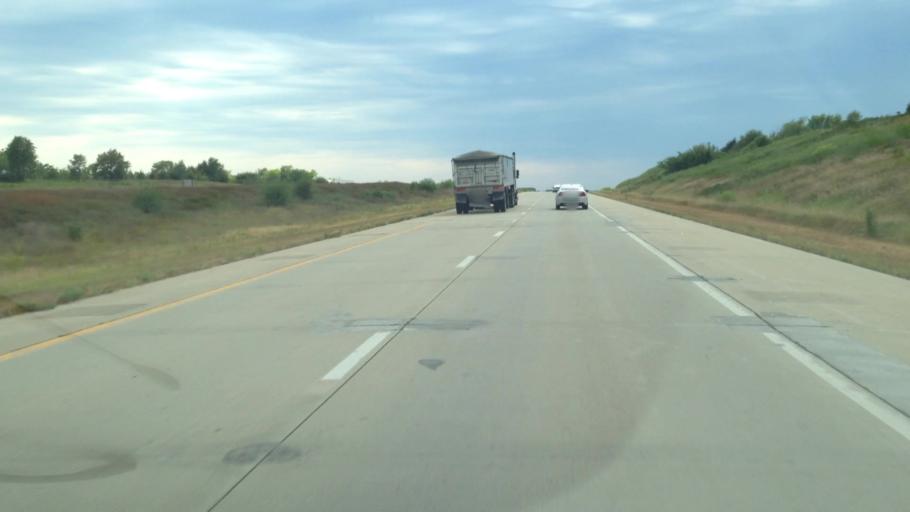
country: US
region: Kansas
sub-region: Franklin County
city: Ottawa
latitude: 38.5646
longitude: -95.3083
